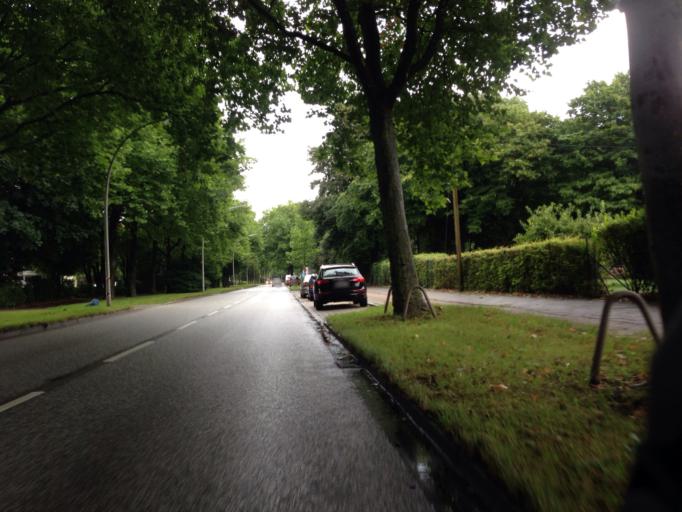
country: DE
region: Hamburg
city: Wandsbek
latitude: 53.5568
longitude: 10.0982
